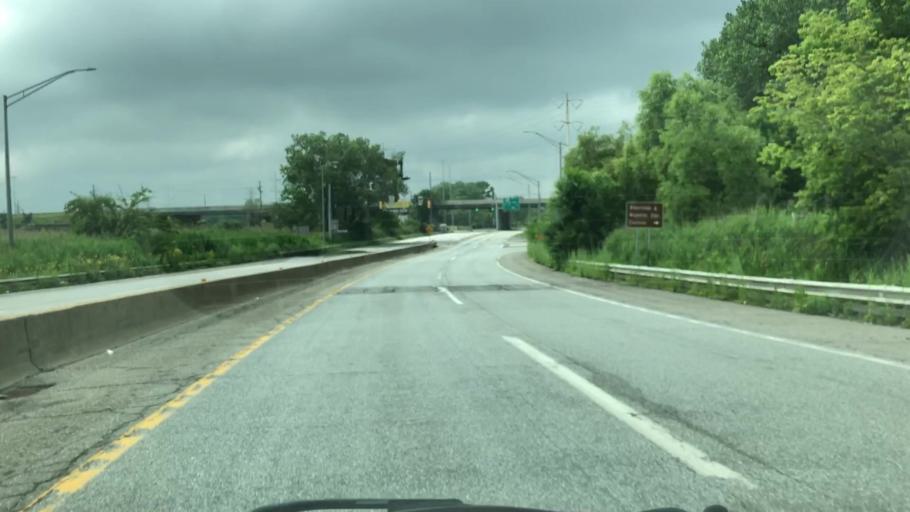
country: US
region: Indiana
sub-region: Lake County
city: East Chicago
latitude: 41.6176
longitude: -87.4290
